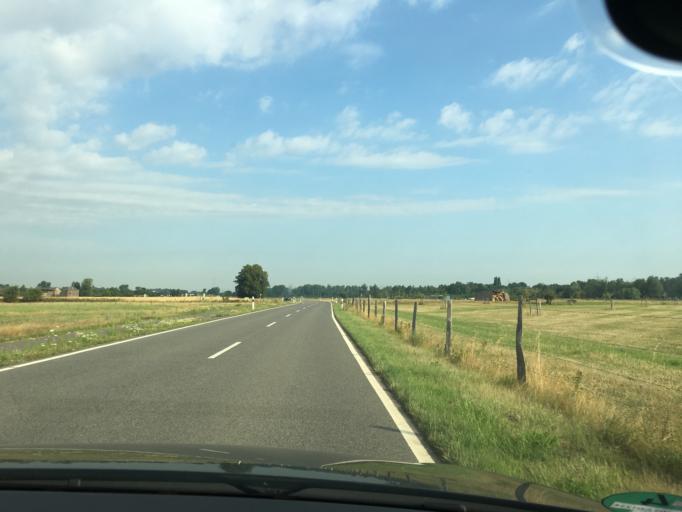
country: DE
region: North Rhine-Westphalia
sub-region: Regierungsbezirk Koln
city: Inden
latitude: 50.8851
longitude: 6.3846
